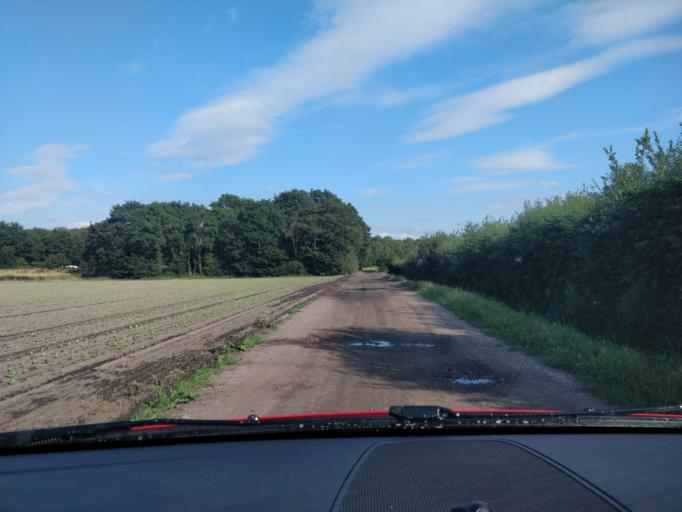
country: GB
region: England
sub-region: Lancashire
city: Banks
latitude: 53.6547
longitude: -2.9019
